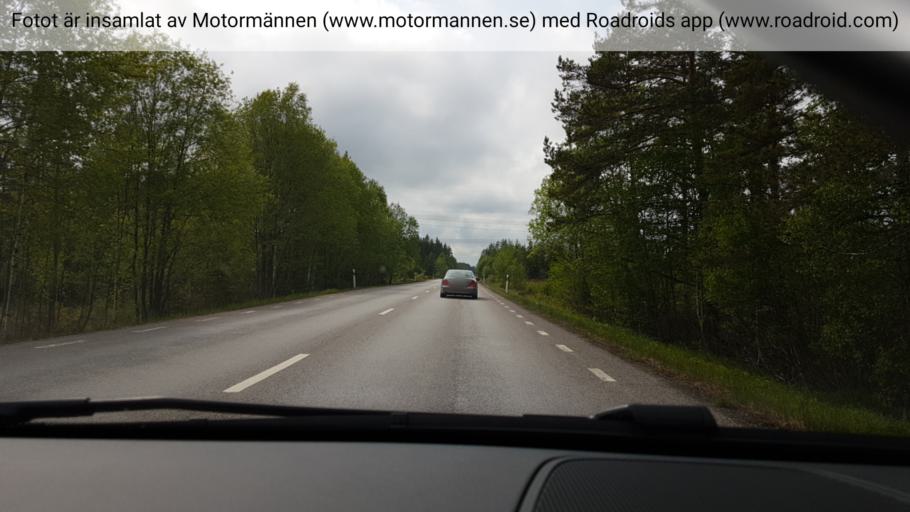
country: SE
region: Uppsala
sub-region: Osthammars Kommun
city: Osterbybruk
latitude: 60.1617
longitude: 18.0244
